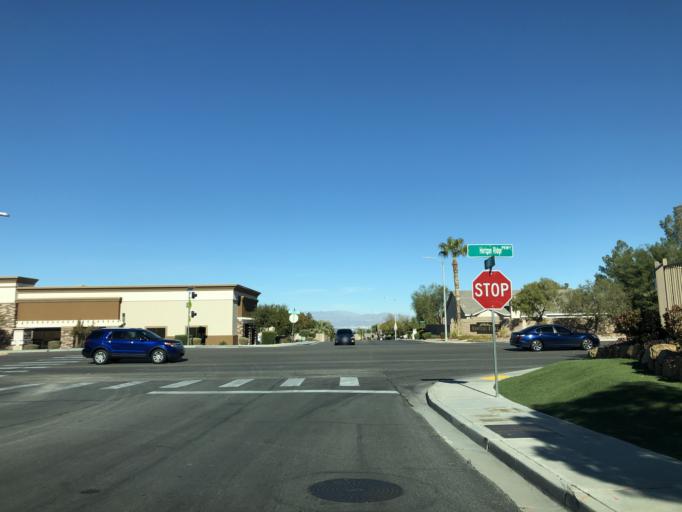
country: US
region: Nevada
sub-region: Clark County
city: Whitney
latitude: 36.0055
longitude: -115.0899
